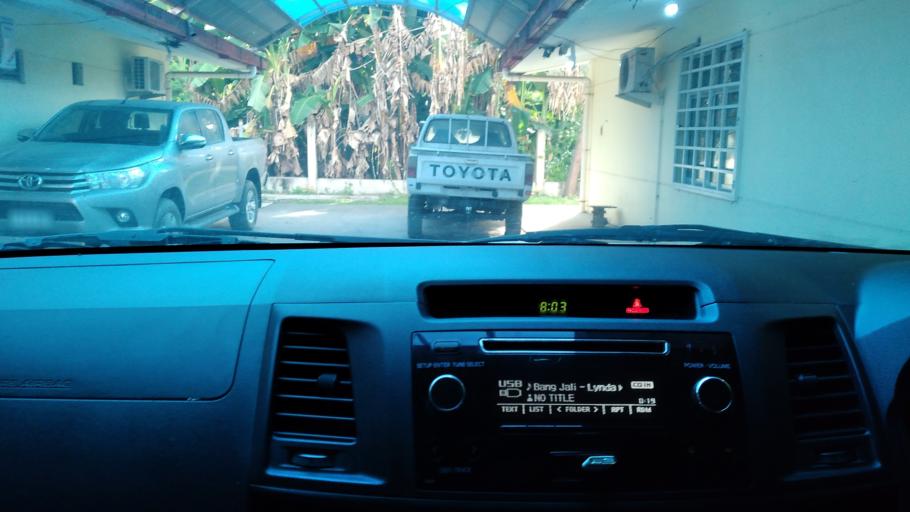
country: TL
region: Dili
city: Dili
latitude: -8.5582
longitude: 125.5746
